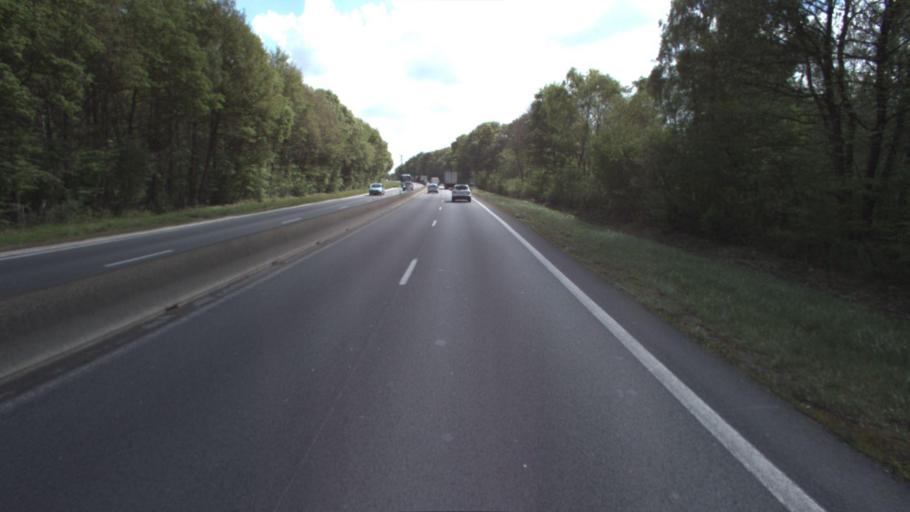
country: FR
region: Ile-de-France
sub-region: Departement de Seine-et-Marne
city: Gretz-Armainvilliers
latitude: 48.7333
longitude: 2.7159
